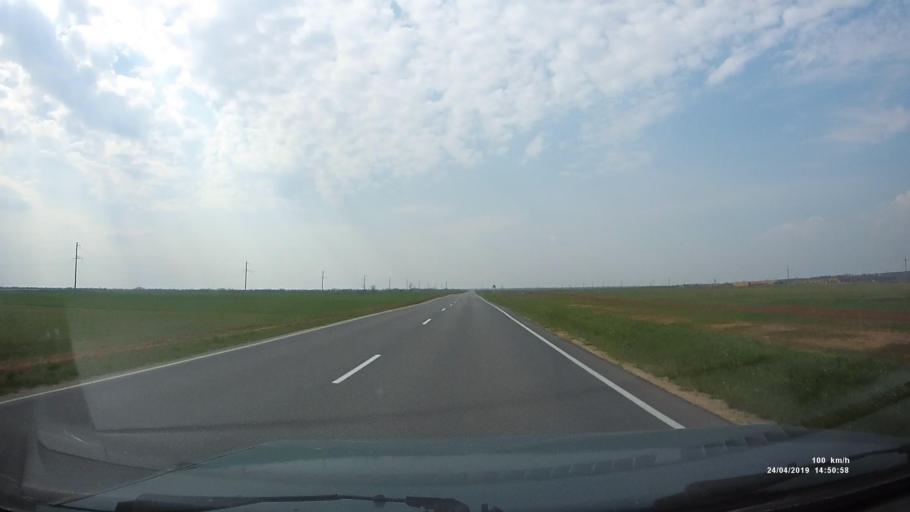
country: RU
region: Rostov
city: Remontnoye
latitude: 46.5212
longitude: 43.7101
